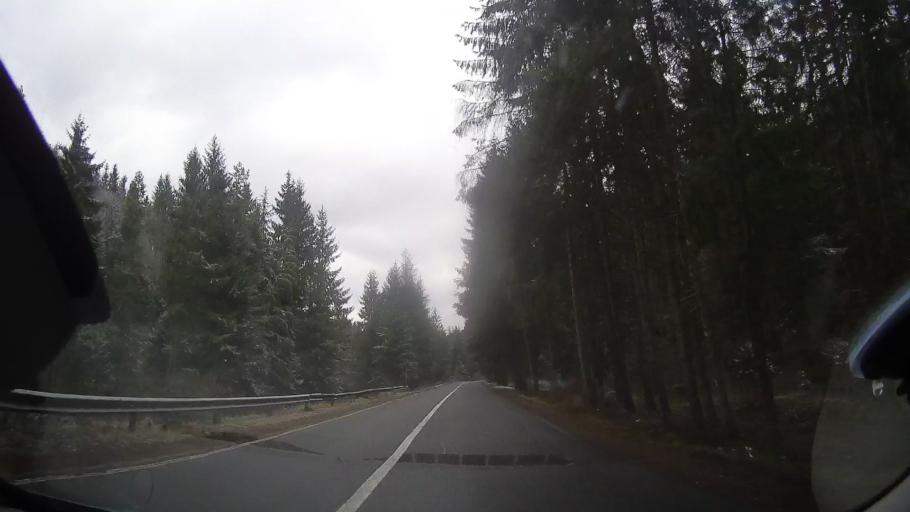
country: RO
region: Cluj
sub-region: Comuna Calatele
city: Calatele
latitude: 46.7414
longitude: 23.0157
